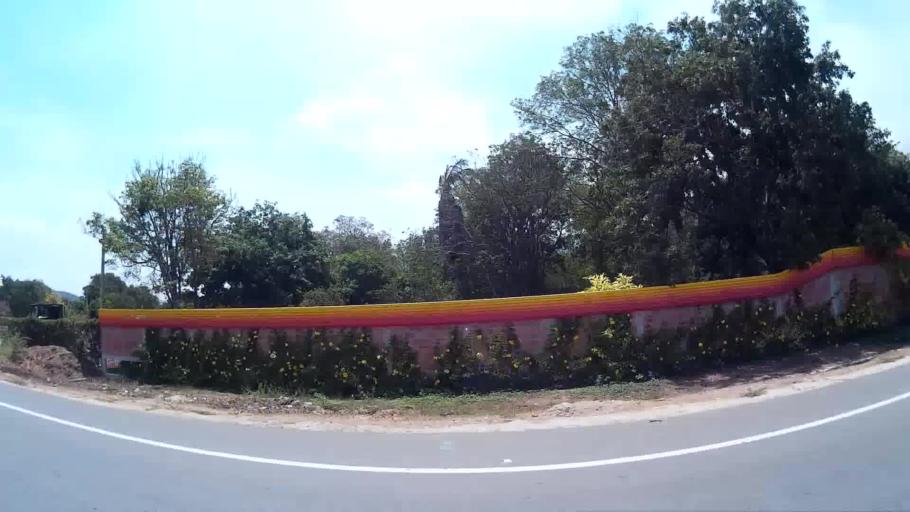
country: CO
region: Magdalena
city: Santa Marta
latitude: 11.1535
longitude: -74.2224
